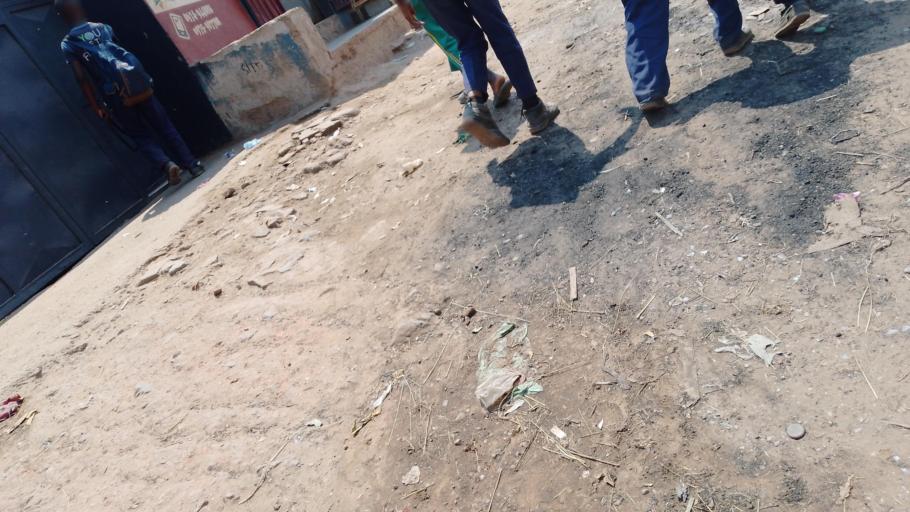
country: ZM
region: Lusaka
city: Lusaka
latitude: -15.3994
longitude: 28.3675
